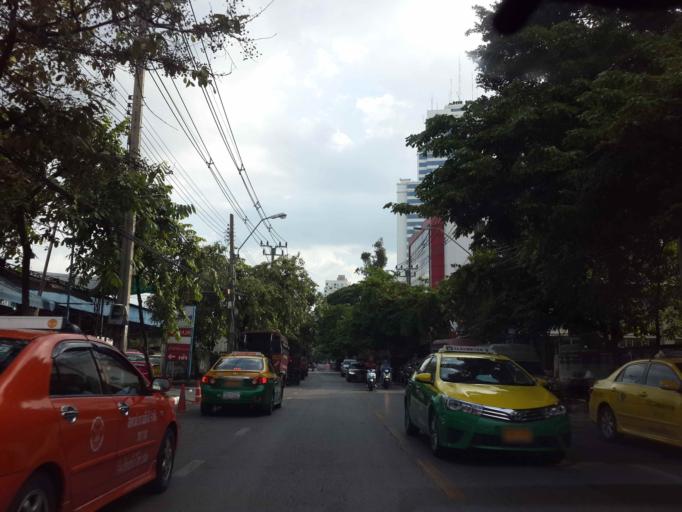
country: TH
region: Bangkok
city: Yan Nawa
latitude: 13.7093
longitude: 100.5407
